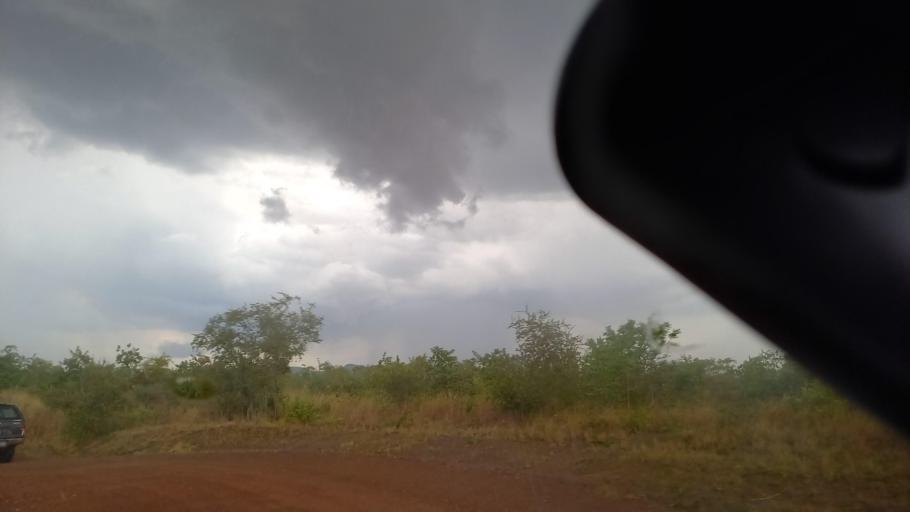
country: ZM
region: Lusaka
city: Kafue
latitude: -15.8648
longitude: 28.1793
